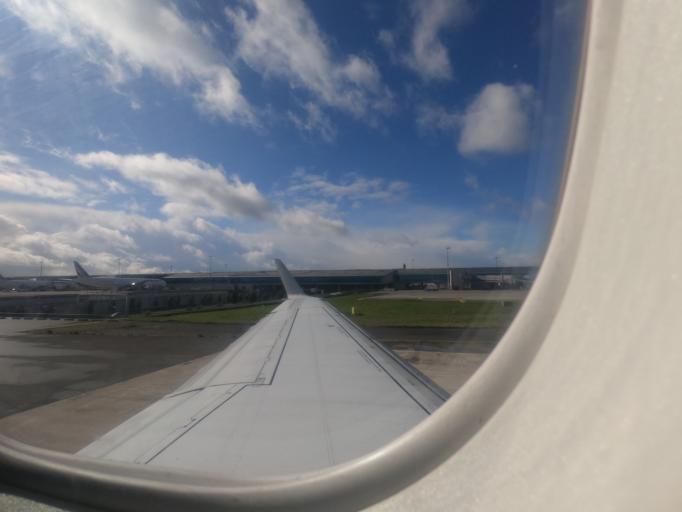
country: FR
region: Ile-de-France
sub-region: Departement de Seine-et-Marne
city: Mitry-Mory
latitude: 49.0058
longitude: 2.5943
